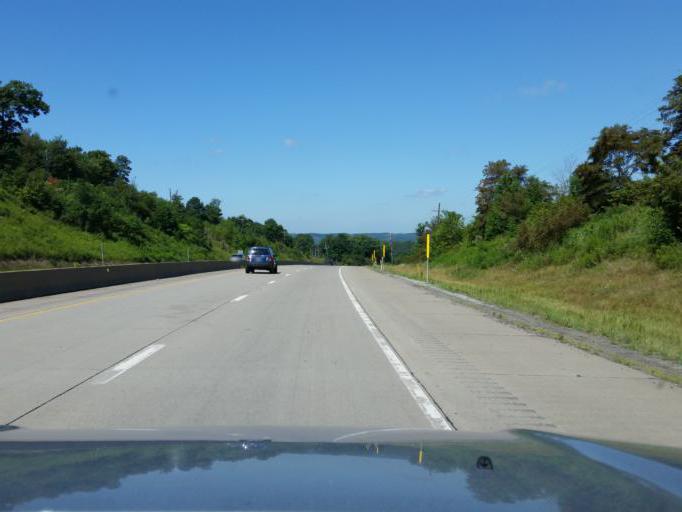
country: US
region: Pennsylvania
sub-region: Cambria County
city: Vinco
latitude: 40.4425
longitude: -78.9627
